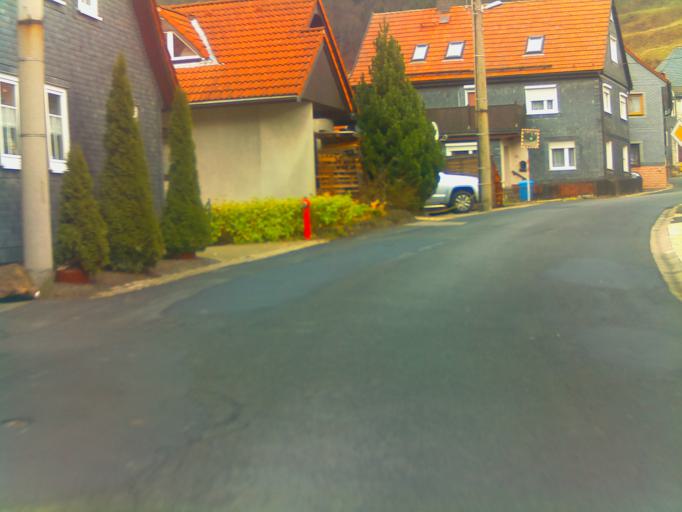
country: DE
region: Thuringia
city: Neustadt am Rennsteig
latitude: 50.5359
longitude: 10.9185
